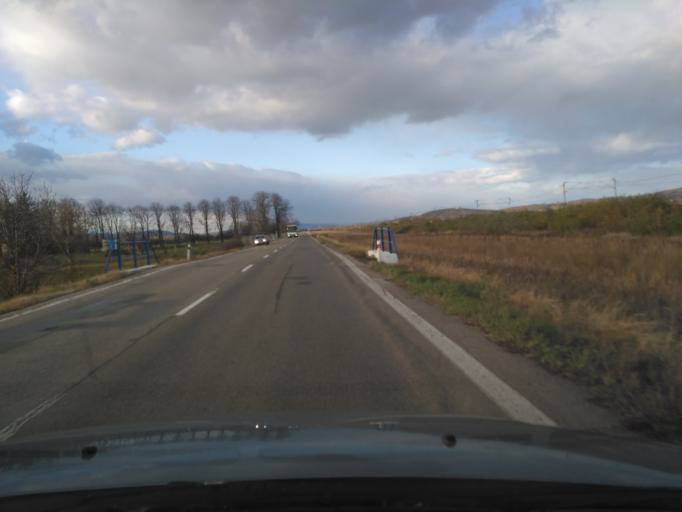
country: HU
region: Borsod-Abauj-Zemplen
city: Satoraljaujhely
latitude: 48.4141
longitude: 21.6651
